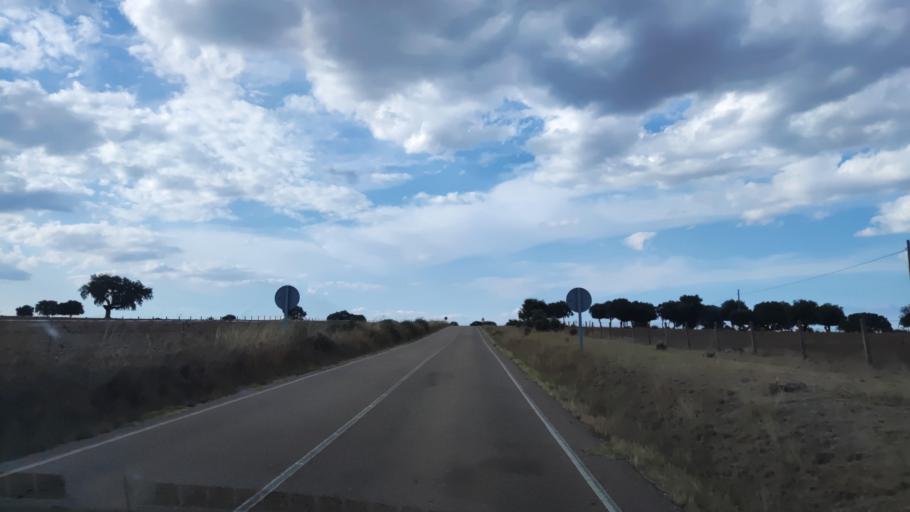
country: ES
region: Castille and Leon
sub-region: Provincia de Salamanca
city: Martiago
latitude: 40.4824
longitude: -6.4929
